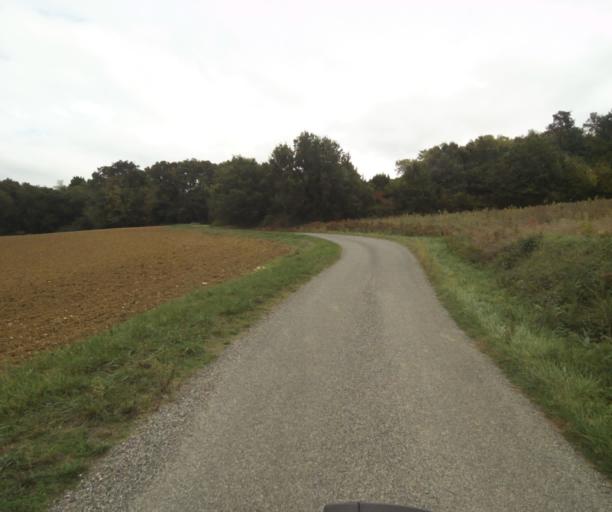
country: FR
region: Midi-Pyrenees
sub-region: Departement du Tarn-et-Garonne
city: Verdun-sur-Garonne
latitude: 43.8453
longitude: 1.1184
